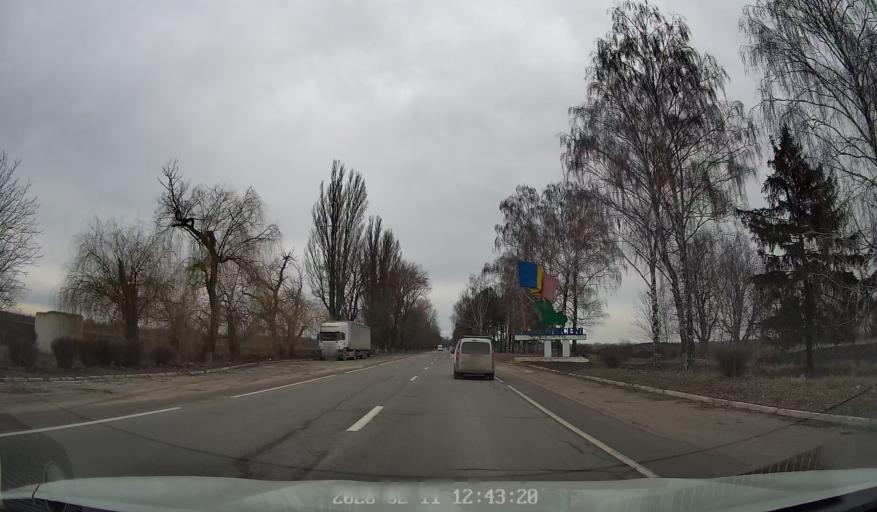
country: MD
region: Raionul Edinet
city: Edinet
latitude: 48.2318
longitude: 27.2116
